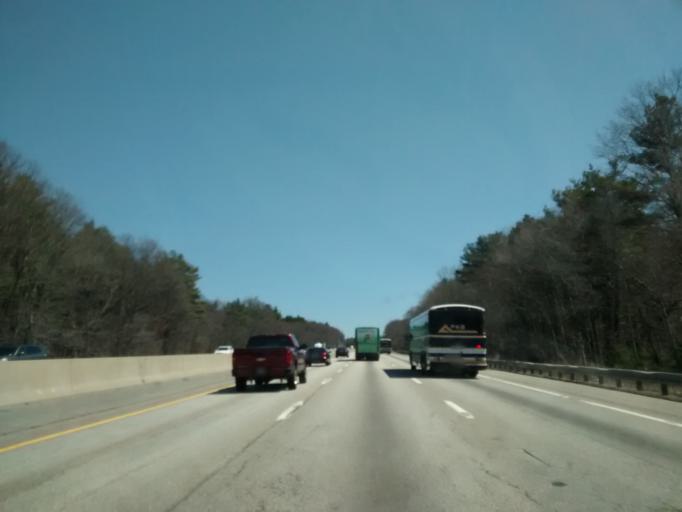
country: US
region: Massachusetts
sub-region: Worcester County
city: Grafton
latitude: 42.2271
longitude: -71.6812
